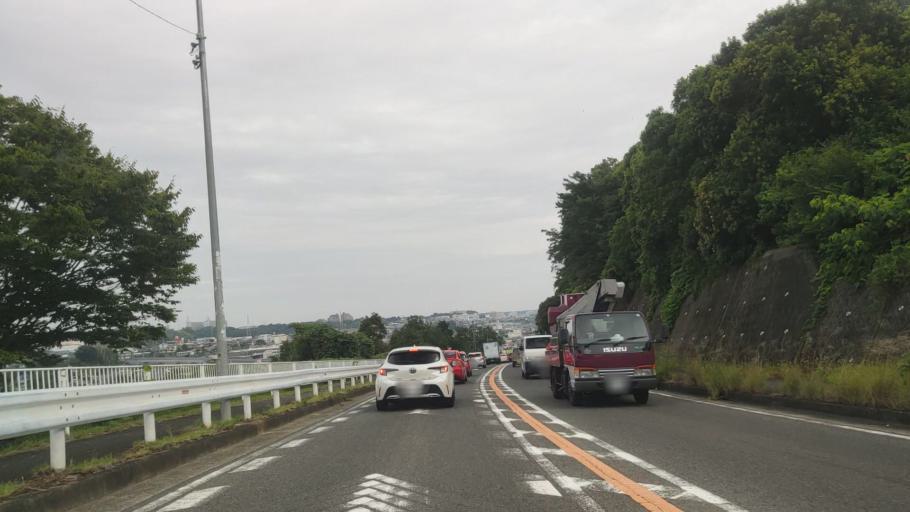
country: JP
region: Osaka
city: Tondabayashicho
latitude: 34.4370
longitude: 135.5578
